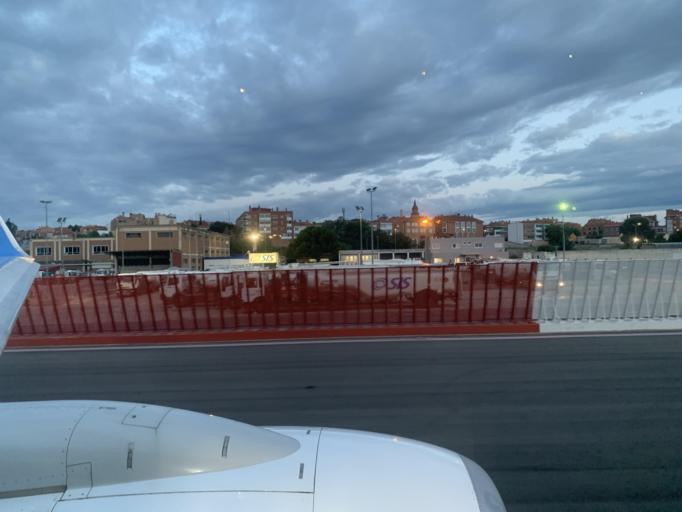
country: ES
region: Madrid
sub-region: Provincia de Madrid
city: Barajas de Madrid
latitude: 40.4733
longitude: -3.5720
